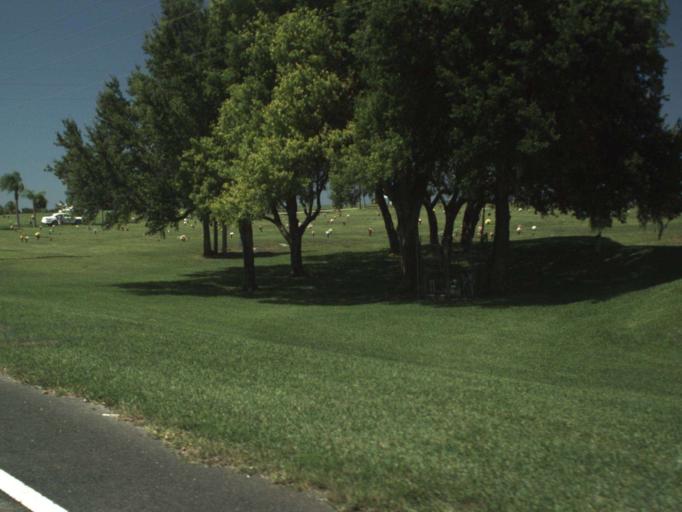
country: US
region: Florida
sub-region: Saint Lucie County
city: Lakewood Park
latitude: 27.5435
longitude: -80.3665
